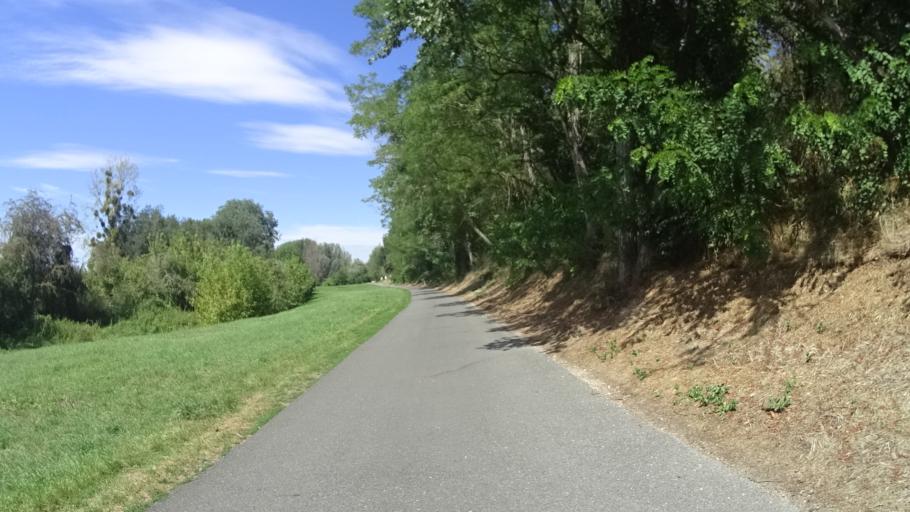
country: FR
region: Centre
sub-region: Departement du Loiret
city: Bonny-sur-Loire
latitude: 47.5716
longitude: 2.8222
